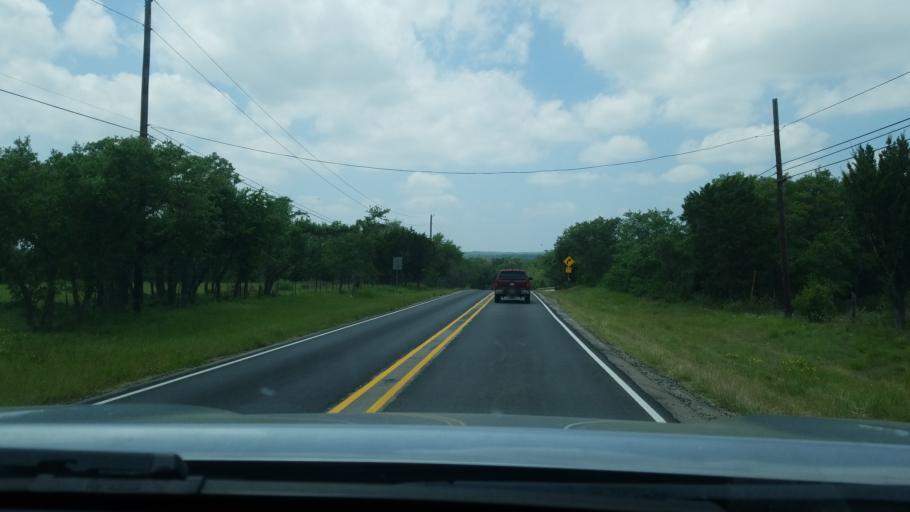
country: US
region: Texas
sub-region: Hays County
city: Dripping Springs
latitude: 30.1596
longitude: -98.0732
